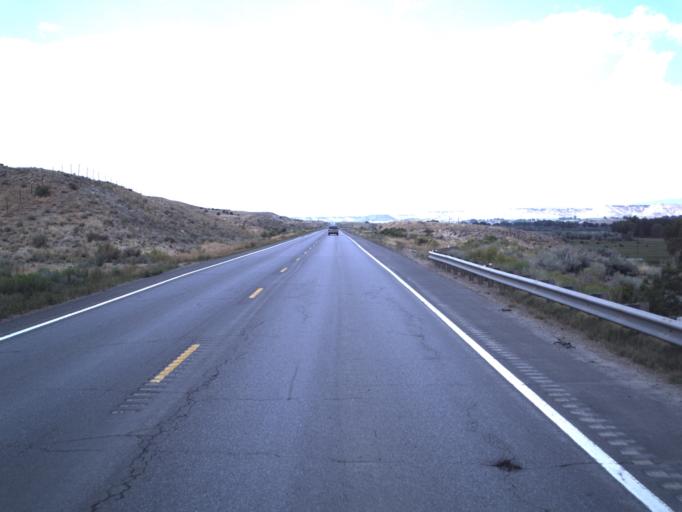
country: US
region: Utah
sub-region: Duchesne County
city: Duchesne
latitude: 40.1598
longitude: -110.2678
